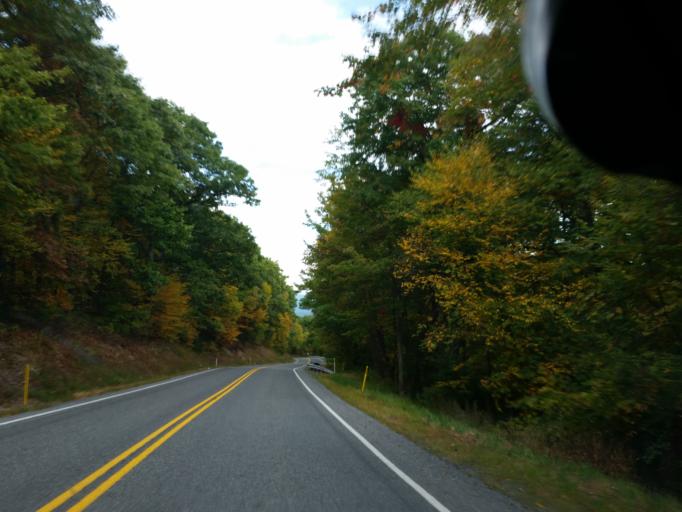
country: US
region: Pennsylvania
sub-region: Lycoming County
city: Duboistown
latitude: 41.1415
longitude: -77.0657
